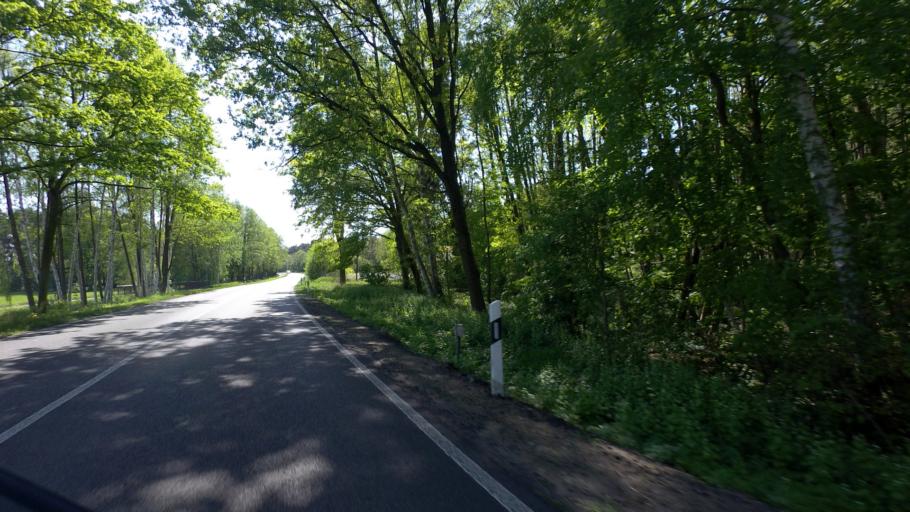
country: DE
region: Brandenburg
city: Tauche
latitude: 52.1391
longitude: 14.2057
